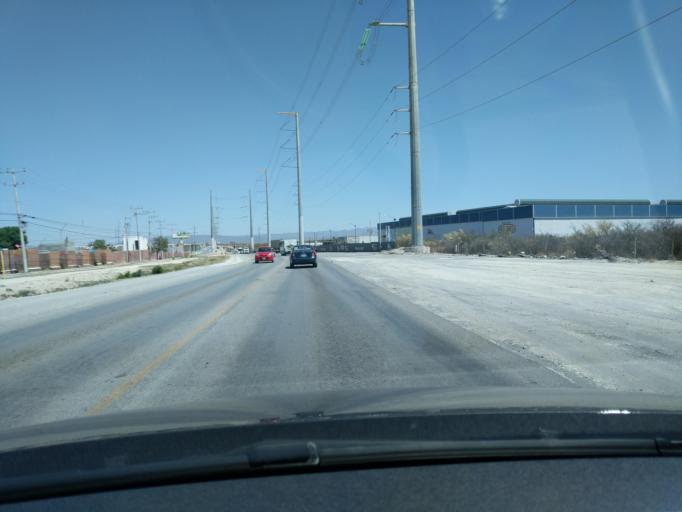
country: MX
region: Nuevo Leon
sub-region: Apodaca
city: Artemio Trevino
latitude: 25.8357
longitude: -100.1388
